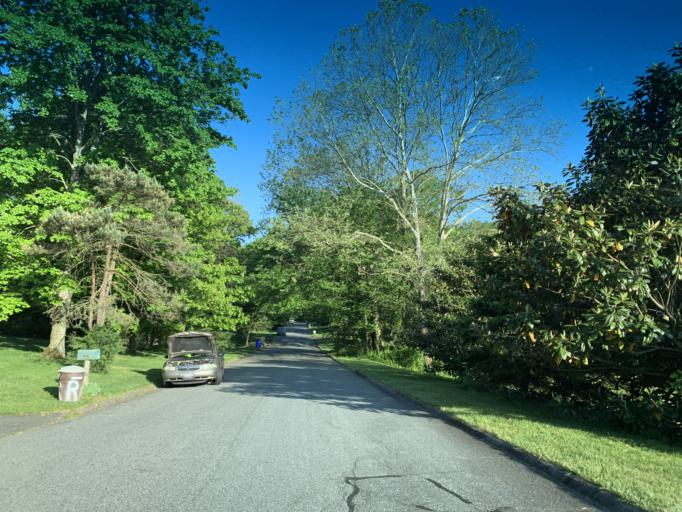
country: US
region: Maryland
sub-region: Harford County
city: Bel Air South
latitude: 39.5092
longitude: -76.2935
